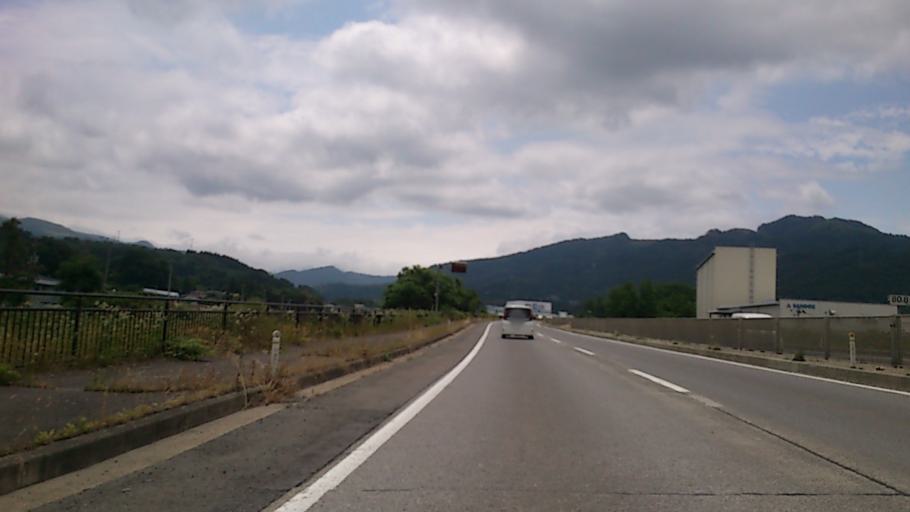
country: JP
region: Yamagata
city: Kaminoyama
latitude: 38.1720
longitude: 140.3052
